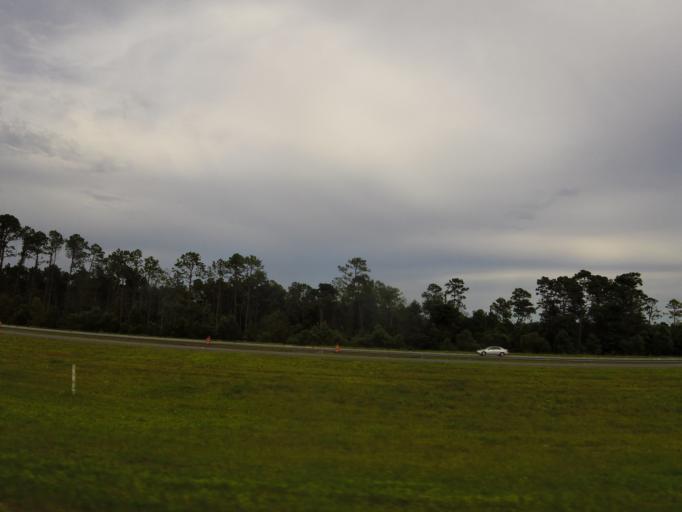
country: US
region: Florida
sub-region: Clay County
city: Lakeside
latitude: 30.1418
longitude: -81.8309
